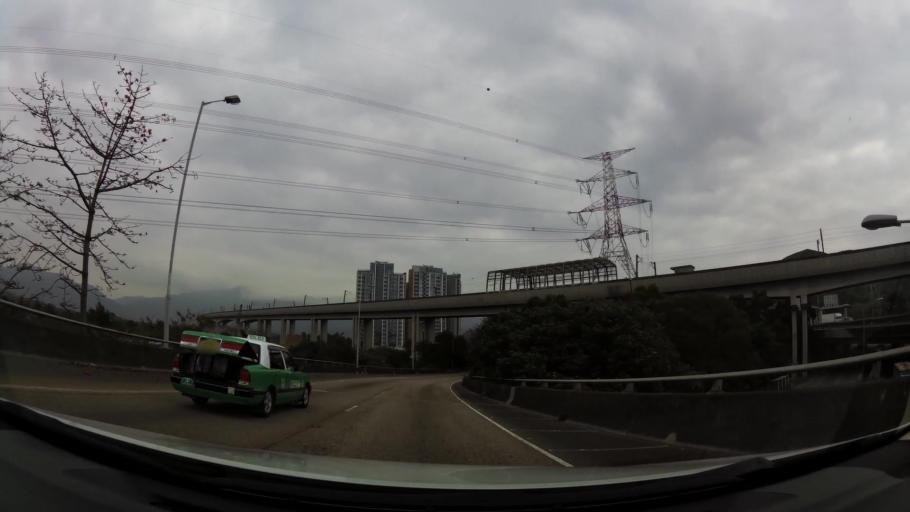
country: HK
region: Yuen Long
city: Yuen Long Kau Hui
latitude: 22.4473
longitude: 114.0497
